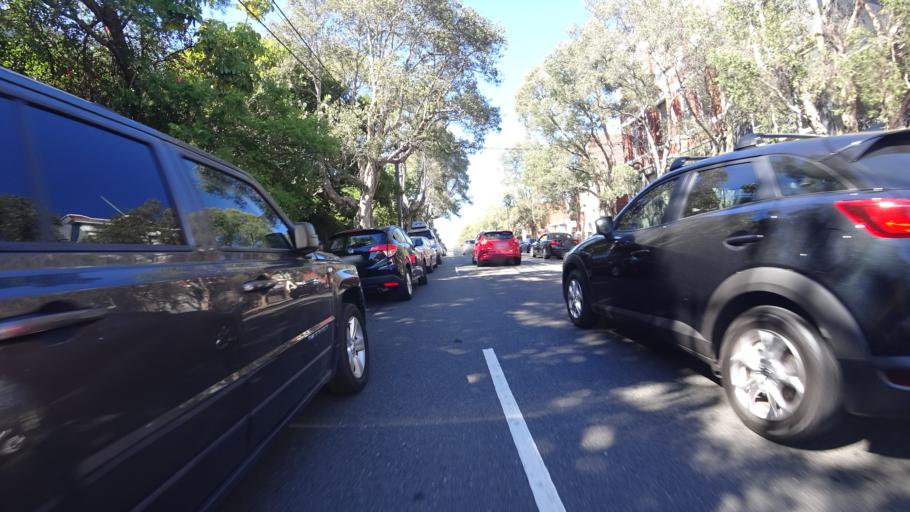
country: AU
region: New South Wales
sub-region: City of Sydney
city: Redfern
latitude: -33.8904
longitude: 151.2078
